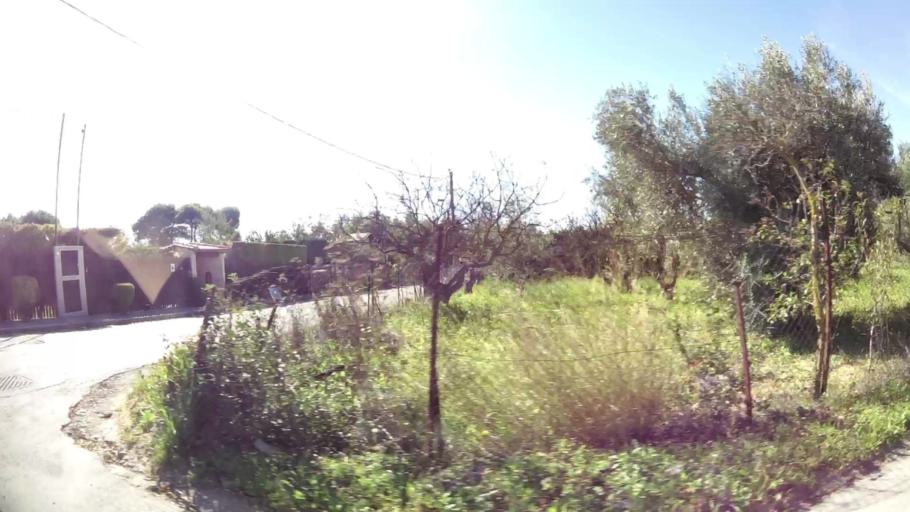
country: GR
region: Attica
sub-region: Nomarchia Anatolikis Attikis
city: Varybobi
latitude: 38.1330
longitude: 23.7852
